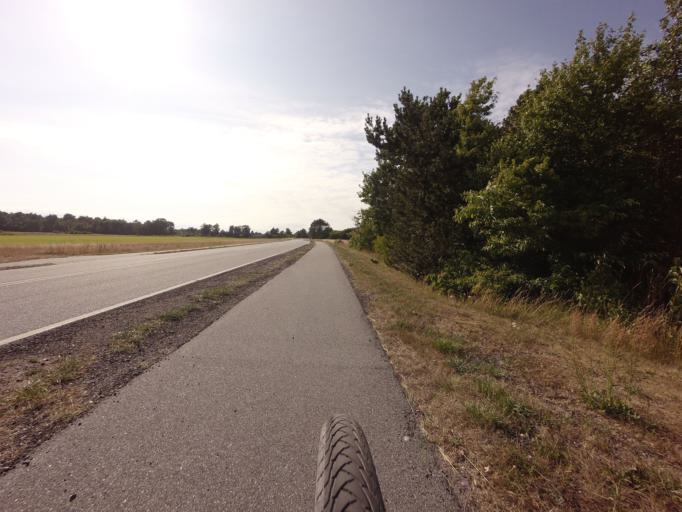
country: DK
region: North Denmark
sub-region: Laeso Kommune
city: Byrum
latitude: 57.2759
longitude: 10.9418
